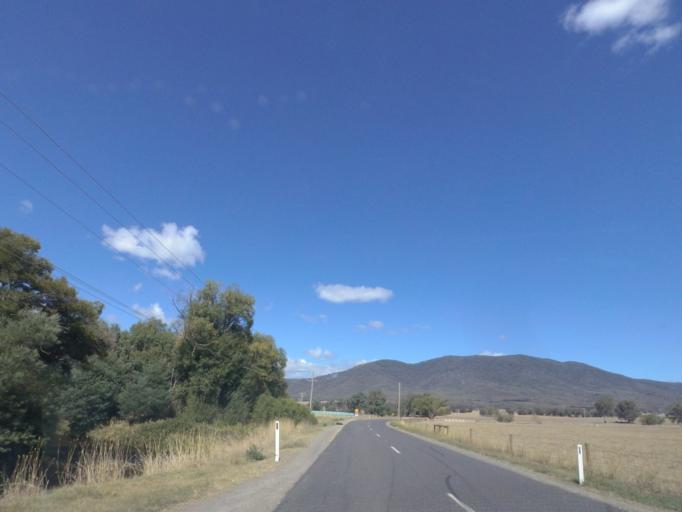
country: AU
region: Victoria
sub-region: Murrindindi
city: Alexandra
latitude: -37.2828
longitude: 145.8018
